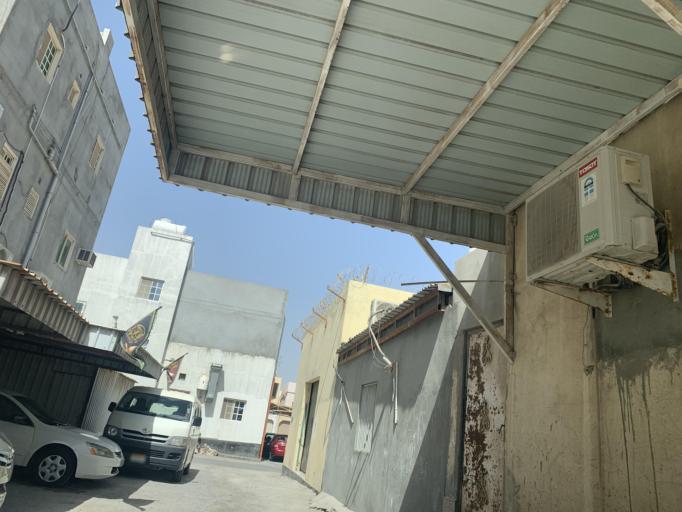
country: BH
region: Northern
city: Sitrah
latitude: 26.1612
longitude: 50.6112
